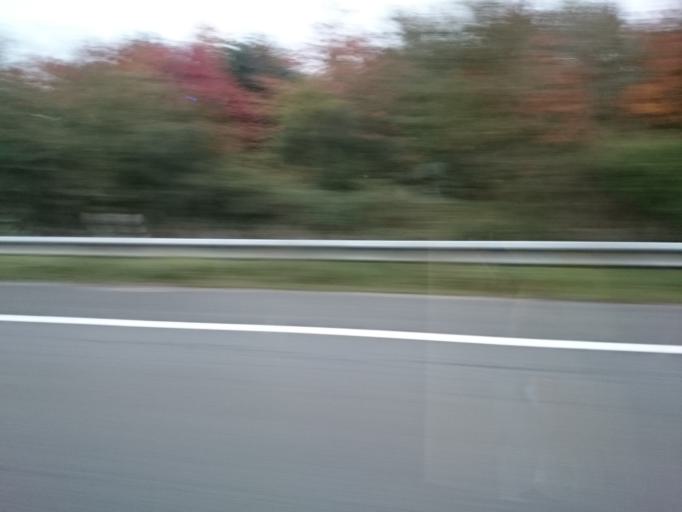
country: FR
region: Pays de la Loire
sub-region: Departement de la Loire-Atlantique
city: Heric
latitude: 47.4021
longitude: -1.6442
